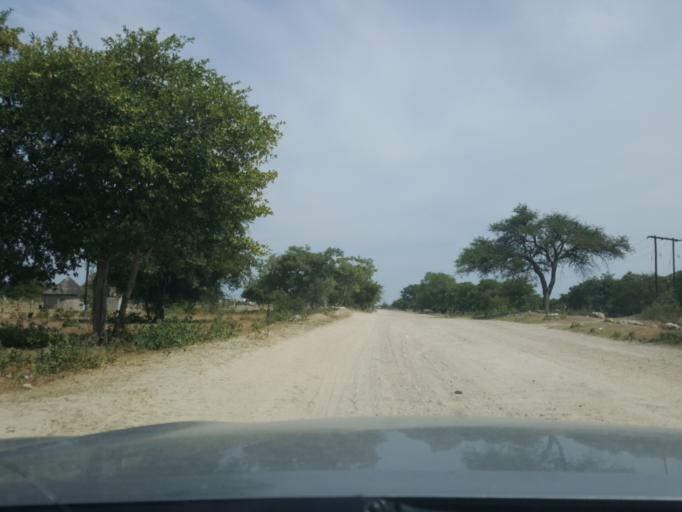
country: BW
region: North West
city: Shakawe
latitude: -18.3110
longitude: 21.8949
